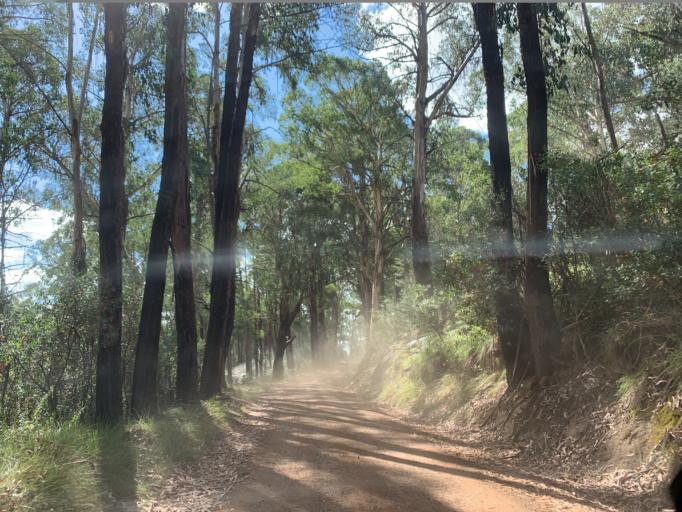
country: AU
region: Victoria
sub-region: Mansfield
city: Mansfield
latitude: -37.0927
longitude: 146.5419
